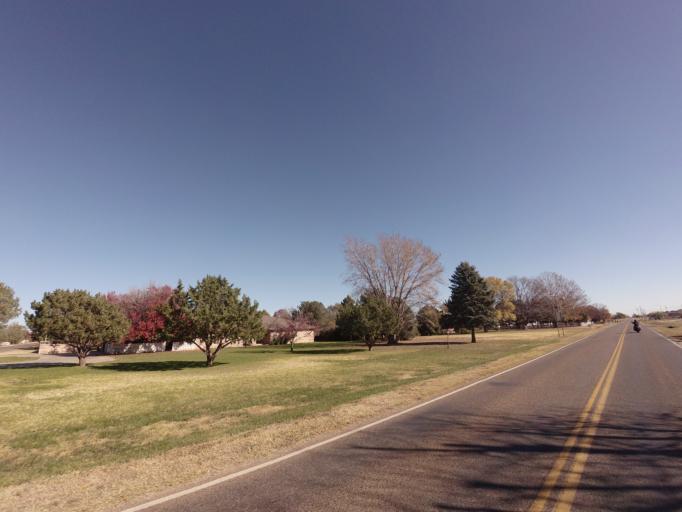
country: US
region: New Mexico
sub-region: Curry County
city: Clovis
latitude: 34.4194
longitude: -103.1742
